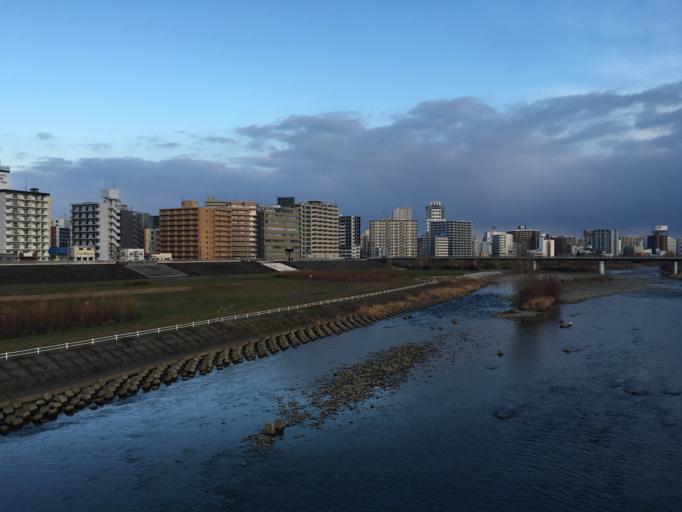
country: JP
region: Hokkaido
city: Sapporo
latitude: 43.0488
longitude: 141.3609
